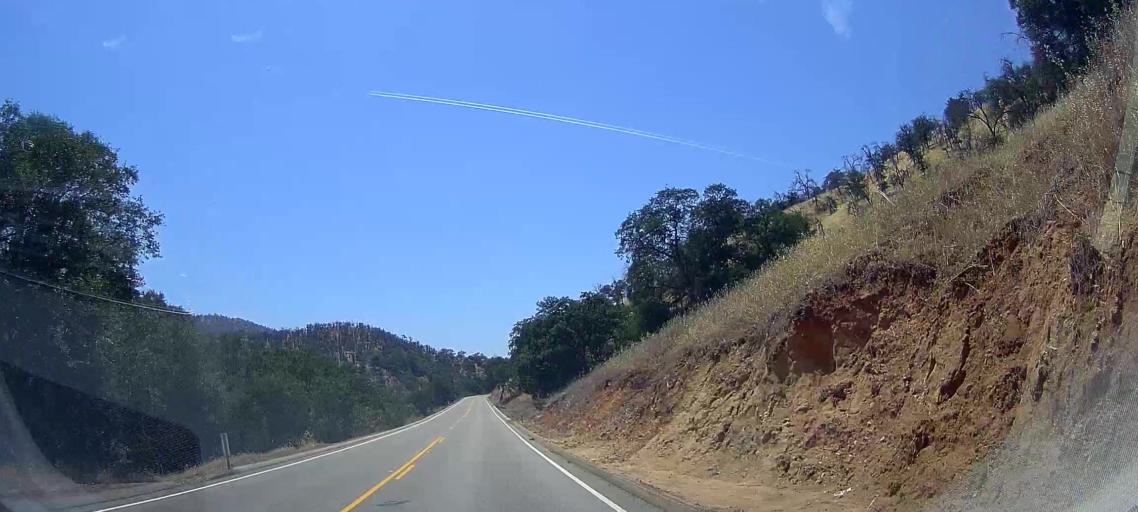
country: US
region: California
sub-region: Fresno County
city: Squaw Valley
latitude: 36.7543
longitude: -119.1859
